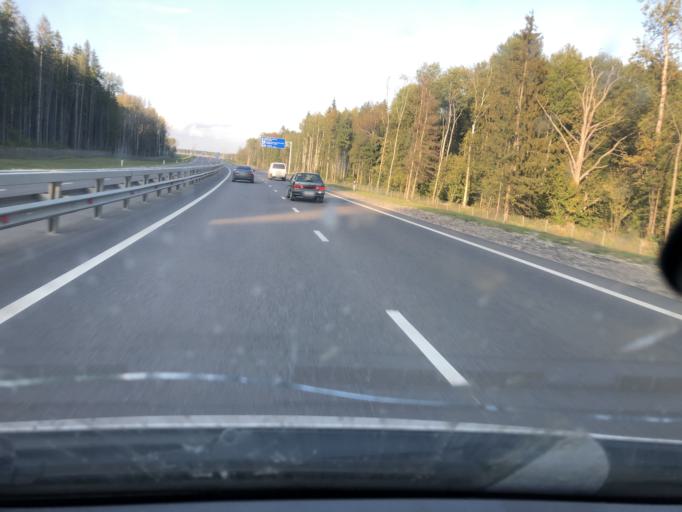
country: RU
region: Kaluga
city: Kaluga
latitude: 54.4512
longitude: 36.2605
